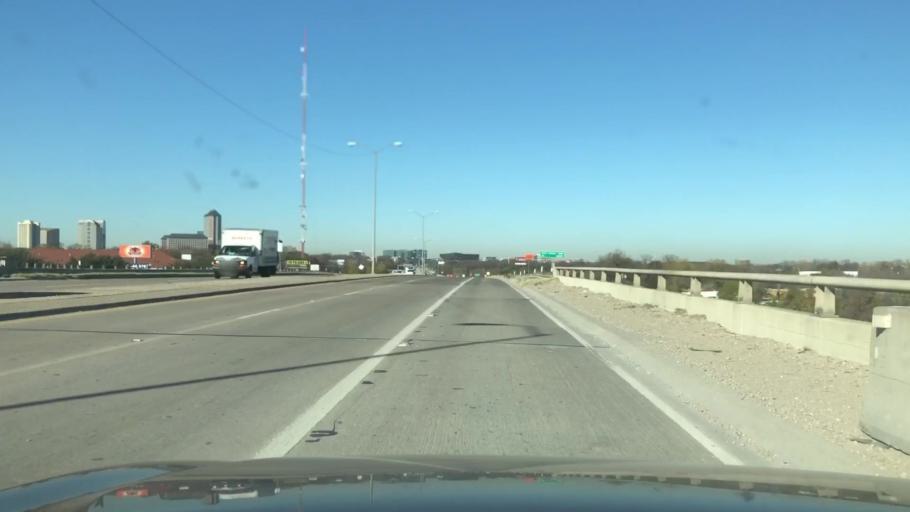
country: US
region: Texas
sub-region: Dallas County
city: Farmers Branch
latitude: 32.8701
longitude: -96.9165
